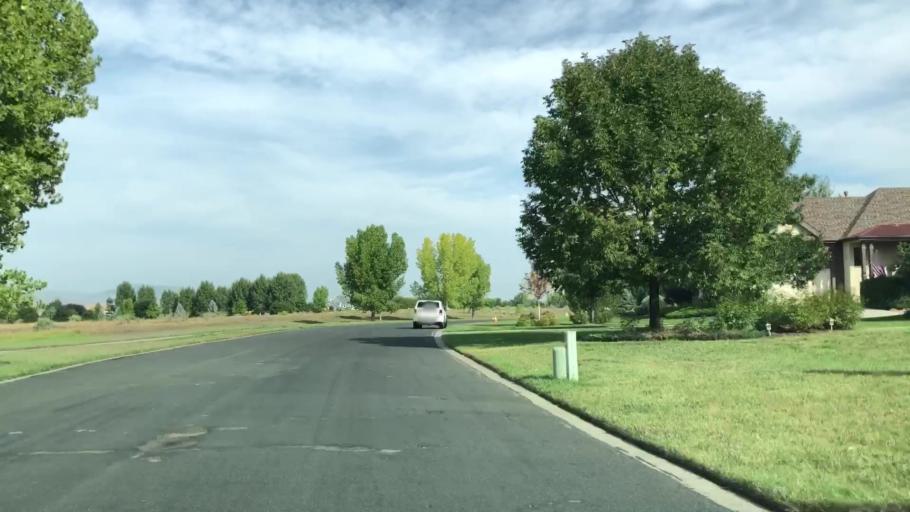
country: US
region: Colorado
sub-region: Larimer County
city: Loveland
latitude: 40.4341
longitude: -105.0526
